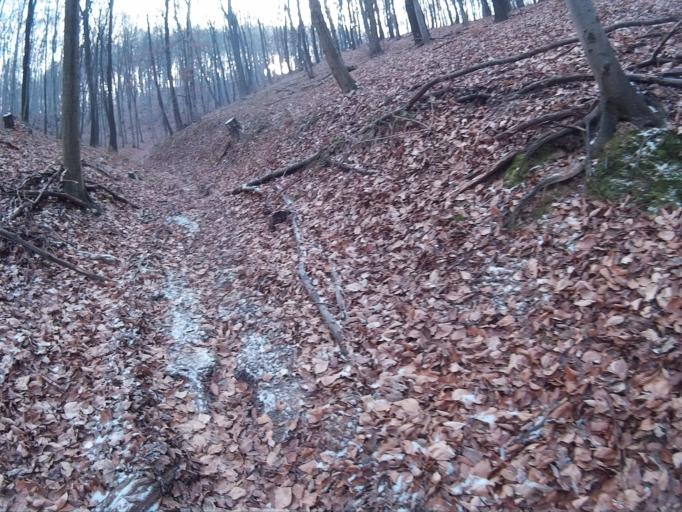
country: HU
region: Komarom-Esztergom
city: Oroszlany
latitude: 47.4668
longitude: 18.3917
